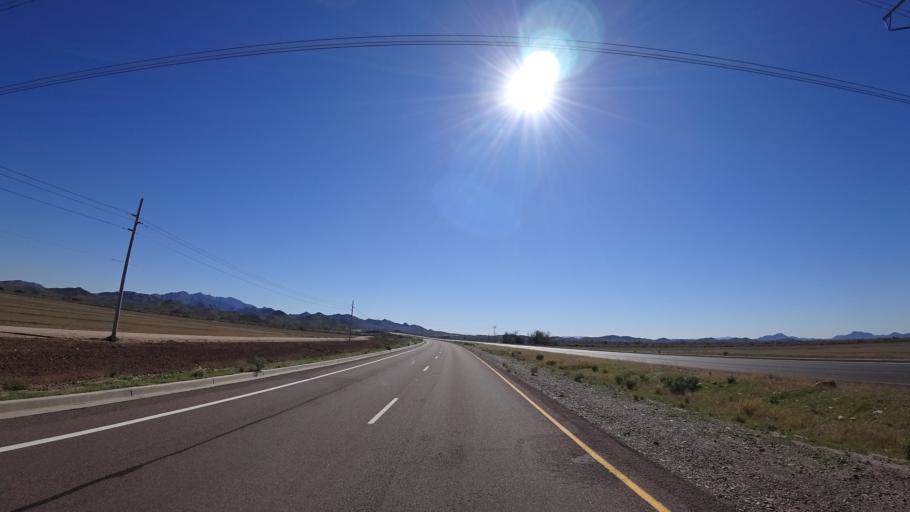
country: US
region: Arizona
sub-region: Maricopa County
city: Goodyear
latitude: 33.3947
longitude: -112.4267
